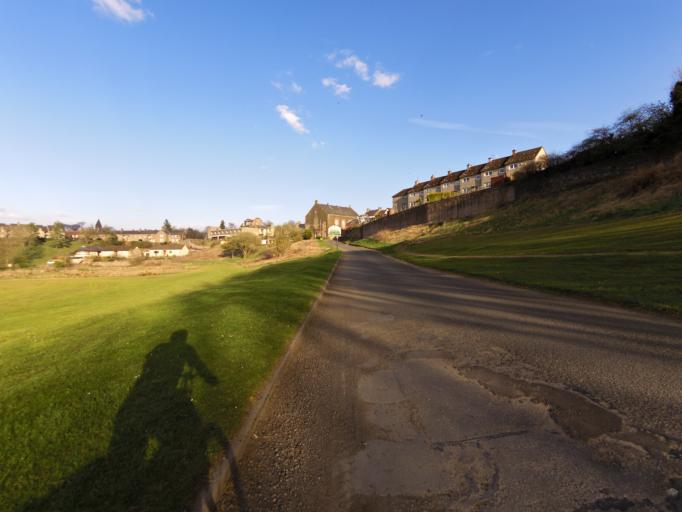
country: GB
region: Scotland
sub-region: Fife
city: Leslie
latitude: 56.2044
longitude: -3.2068
